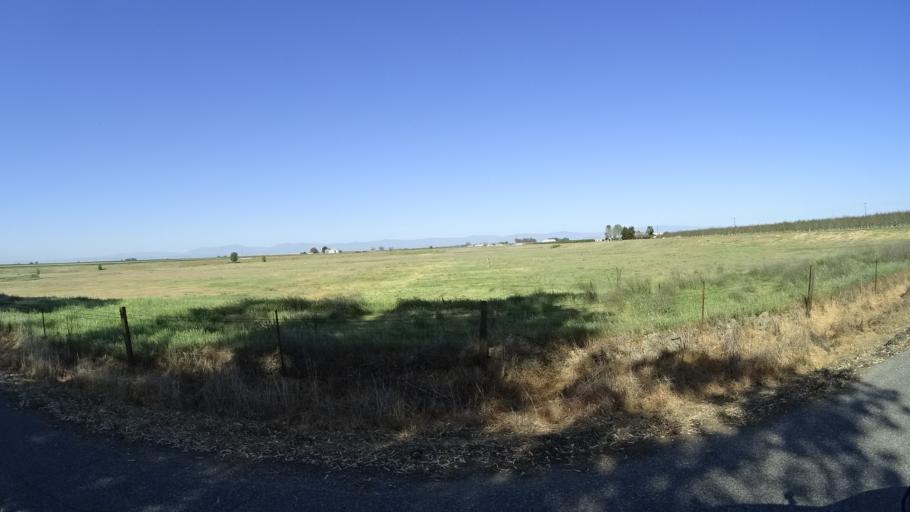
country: US
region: California
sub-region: Glenn County
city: Hamilton City
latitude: 39.6799
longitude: -122.0742
